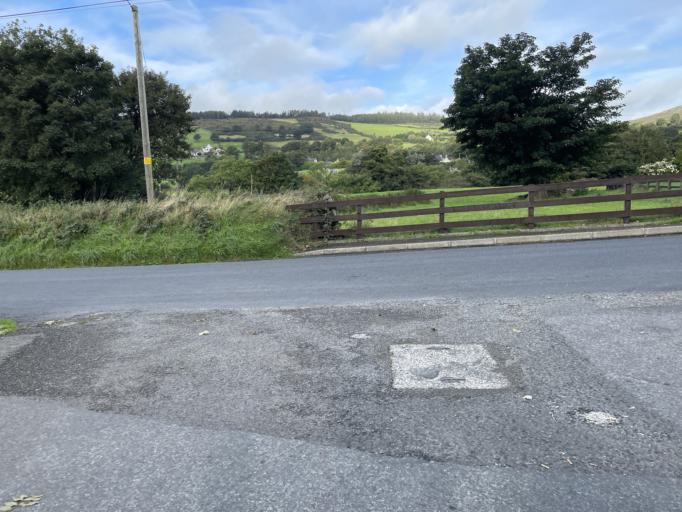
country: GB
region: Northern Ireland
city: Rostrevor
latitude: 54.1086
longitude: -6.1803
